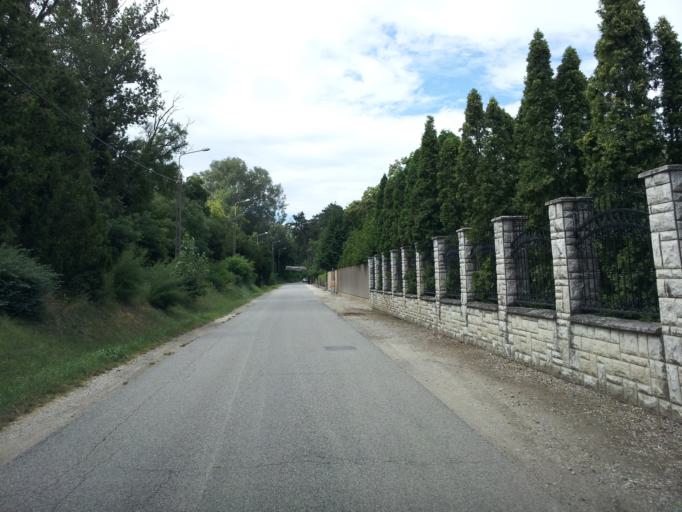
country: HU
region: Somogy
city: Balatonszabadi
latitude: 46.9567
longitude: 18.1509
